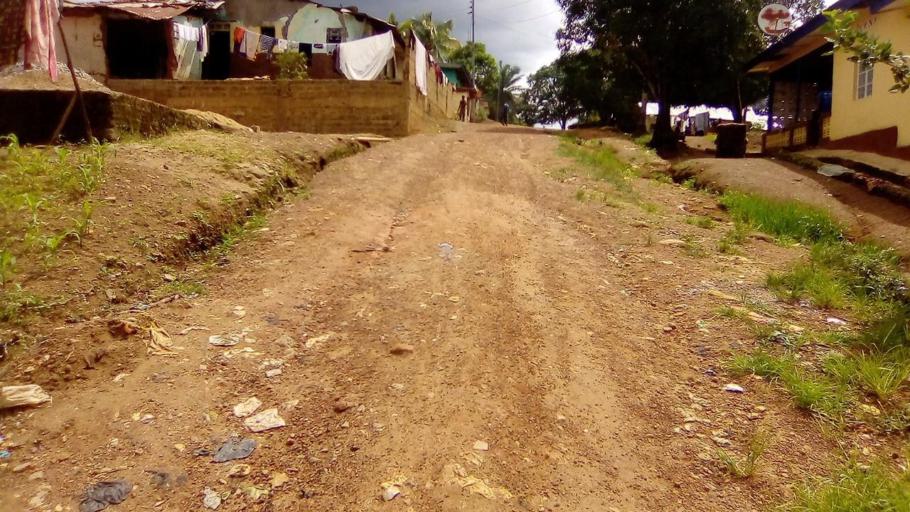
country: SL
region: Southern Province
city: Bo
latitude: 7.9624
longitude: -11.7212
